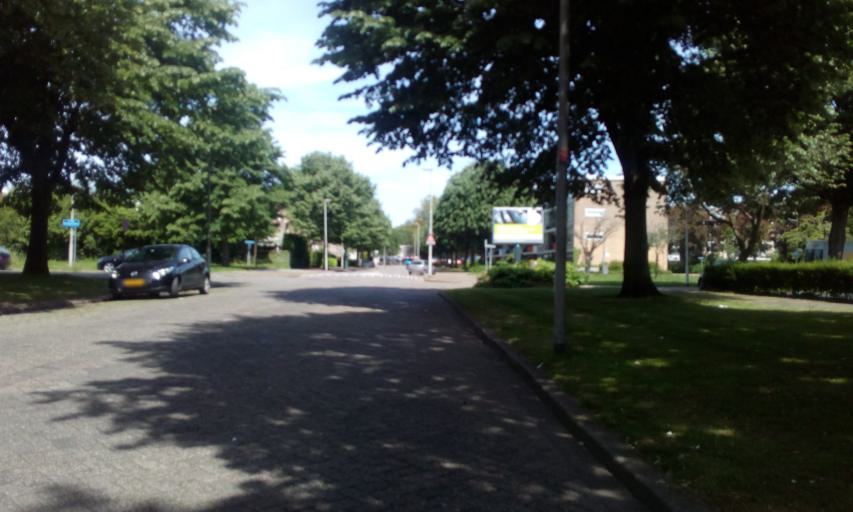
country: NL
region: South Holland
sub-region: Gemeente Rotterdam
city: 's-Gravenland
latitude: 51.9406
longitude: 4.5386
